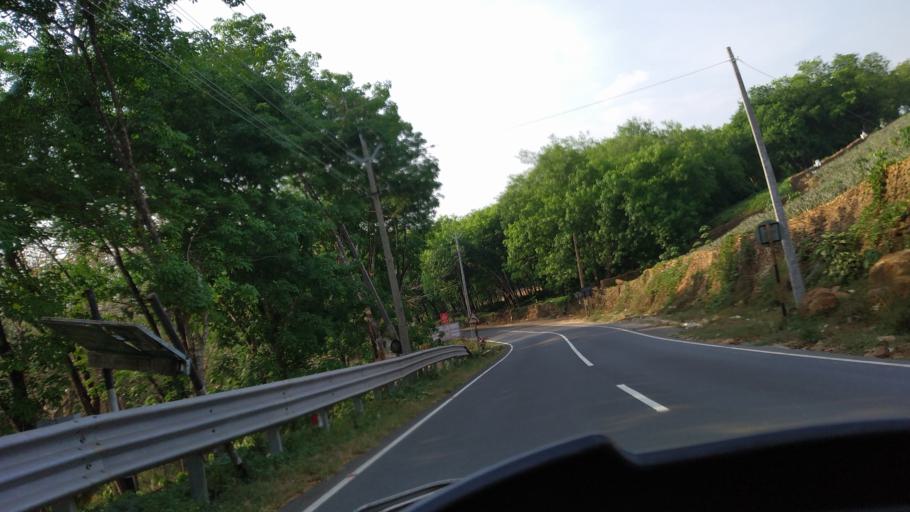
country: IN
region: Kerala
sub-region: Kottayam
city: Erattupetta
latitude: 9.5399
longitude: 76.9052
